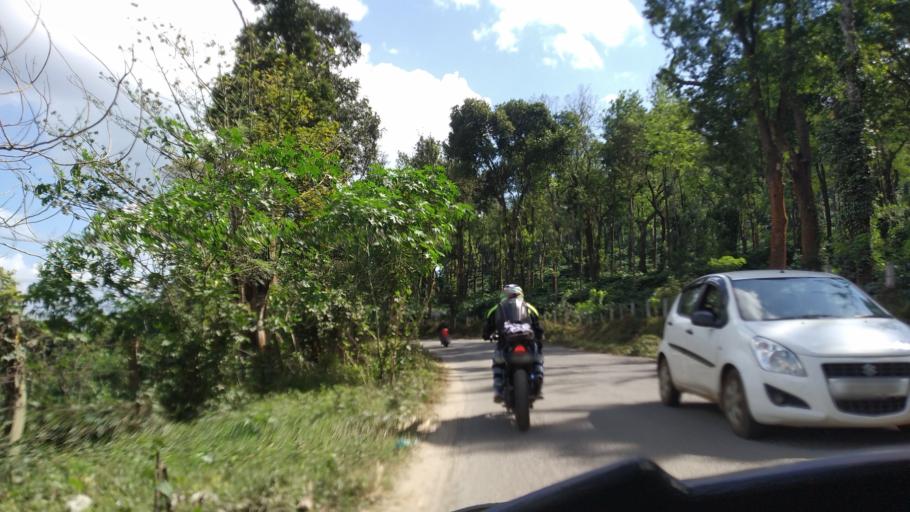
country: IN
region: Karnataka
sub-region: Kodagu
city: Ponnampet
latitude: 11.9622
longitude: 76.0593
